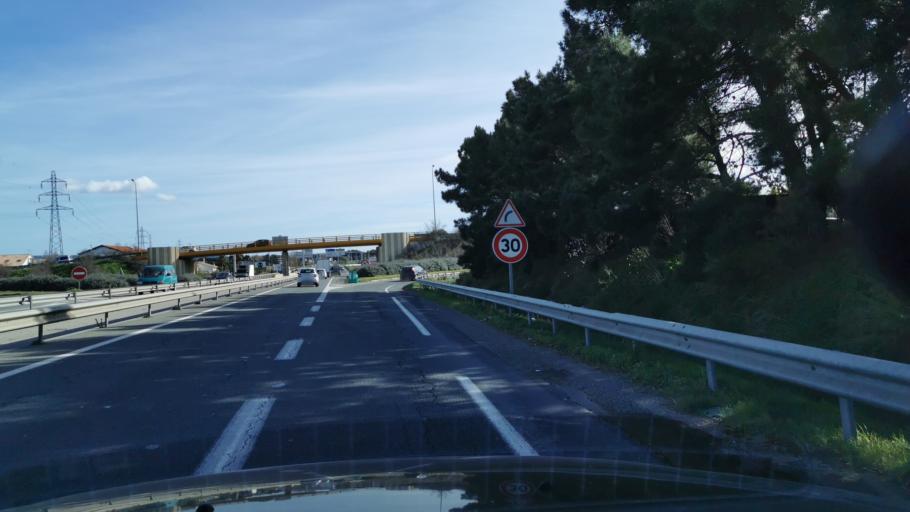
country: FR
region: Languedoc-Roussillon
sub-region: Departement de l'Aude
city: Narbonne
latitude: 43.1692
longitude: 2.9811
